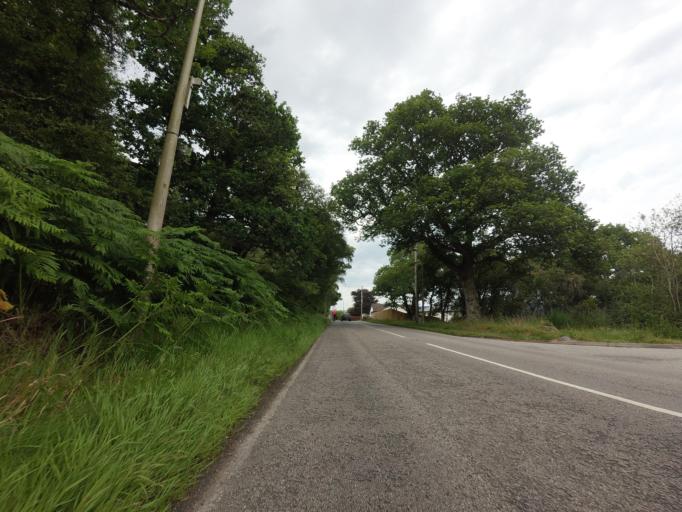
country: GB
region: Scotland
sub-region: Highland
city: Alness
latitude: 57.8779
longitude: -4.3593
